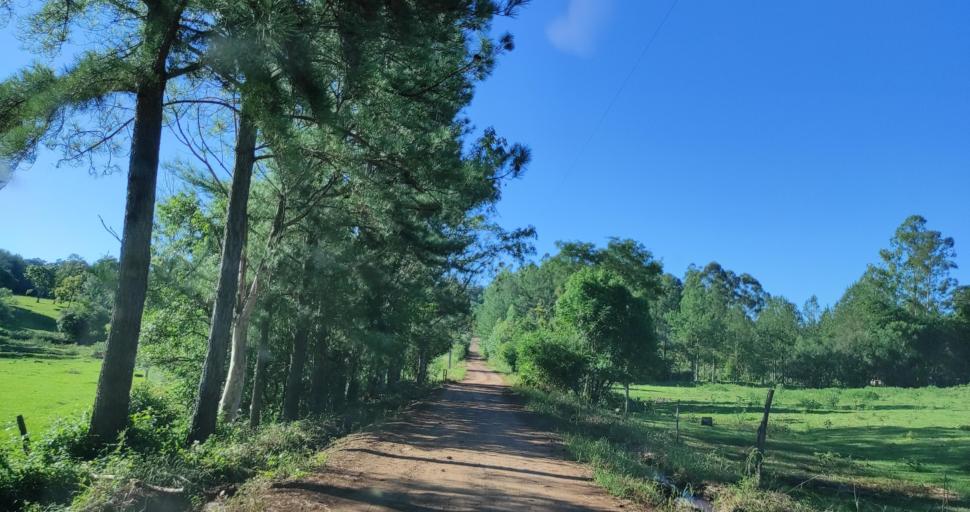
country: AR
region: Misiones
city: Capiovi
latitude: -26.9129
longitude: -54.9995
